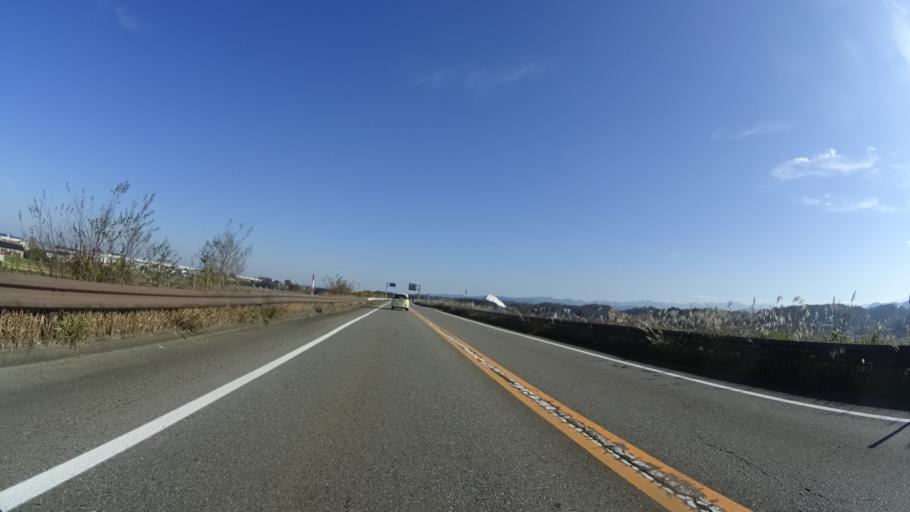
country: JP
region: Ishikawa
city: Komatsu
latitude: 36.3296
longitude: 136.4162
